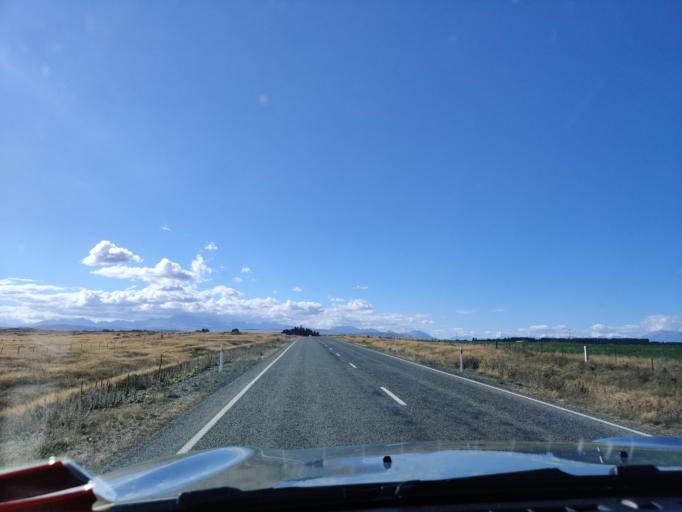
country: NZ
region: Canterbury
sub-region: Timaru District
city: Pleasant Point
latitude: -44.1097
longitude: 170.3529
